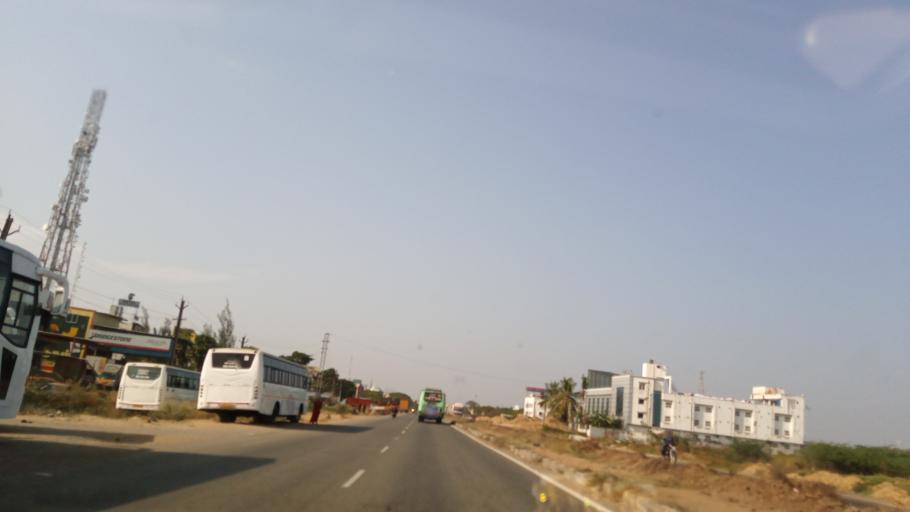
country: IN
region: Tamil Nadu
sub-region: Kancheepuram
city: Sriperumbudur
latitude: 12.9676
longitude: 79.9537
